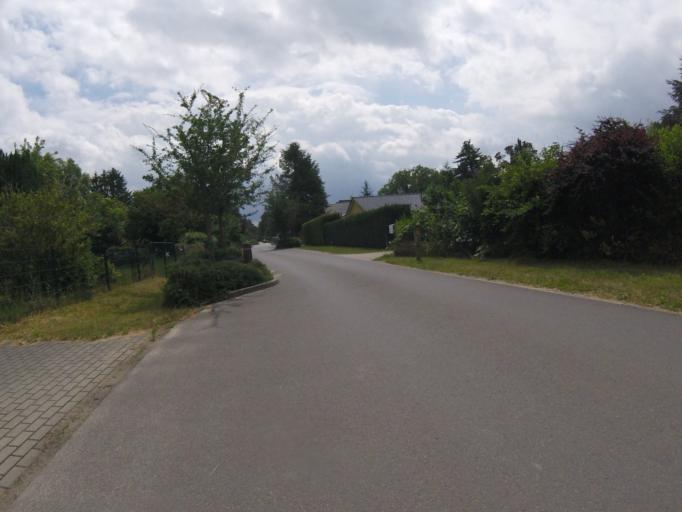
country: DE
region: Brandenburg
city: Bestensee
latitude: 52.2610
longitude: 13.6424
